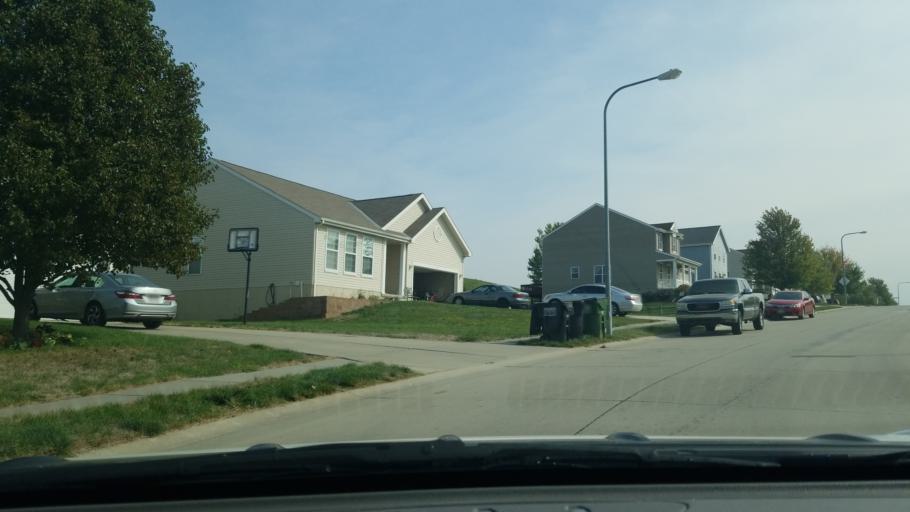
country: US
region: Nebraska
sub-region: Sarpy County
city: Papillion
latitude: 41.1286
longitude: -96.0579
